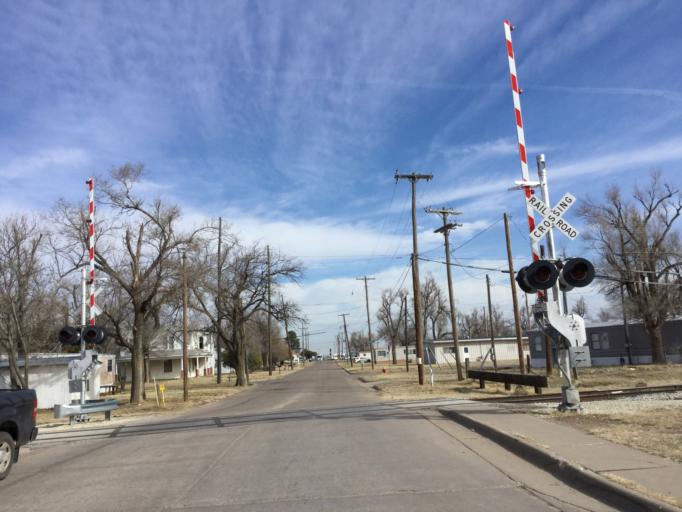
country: US
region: Kansas
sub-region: Barton County
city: Great Bend
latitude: 38.3588
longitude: -98.7508
